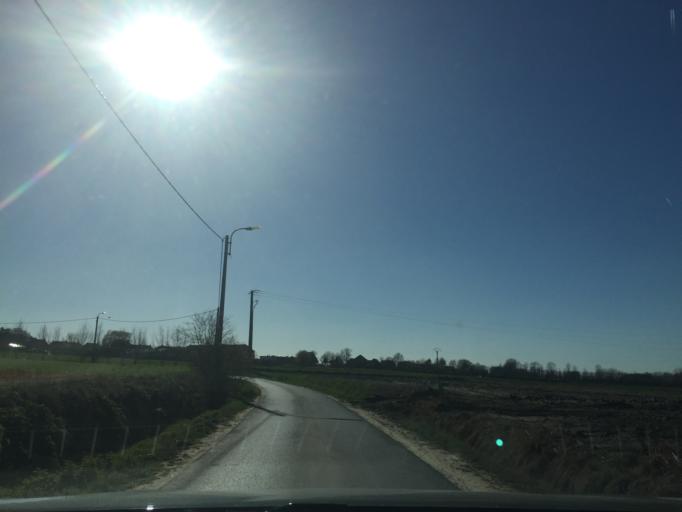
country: BE
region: Flanders
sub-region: Provincie West-Vlaanderen
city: Hooglede
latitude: 50.9845
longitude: 3.0740
